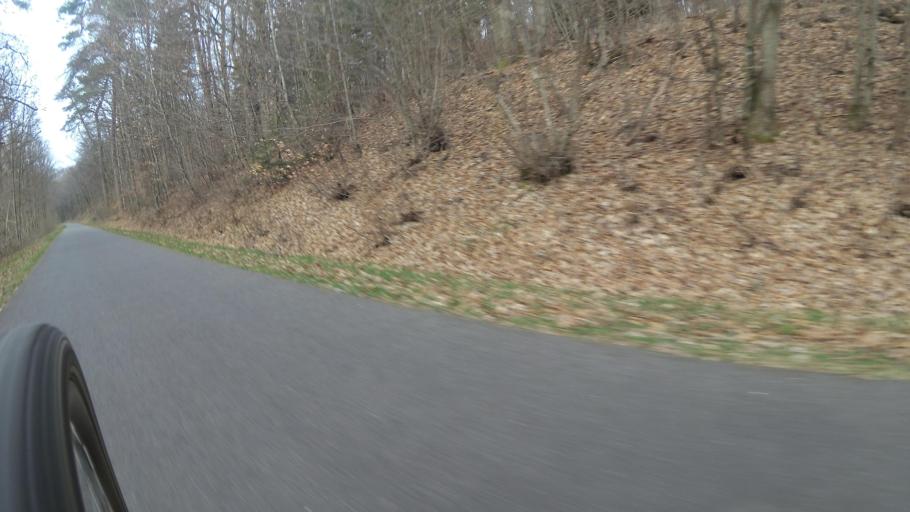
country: DE
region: Rheinland-Pfalz
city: Ellweiler
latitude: 49.6308
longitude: 7.1633
